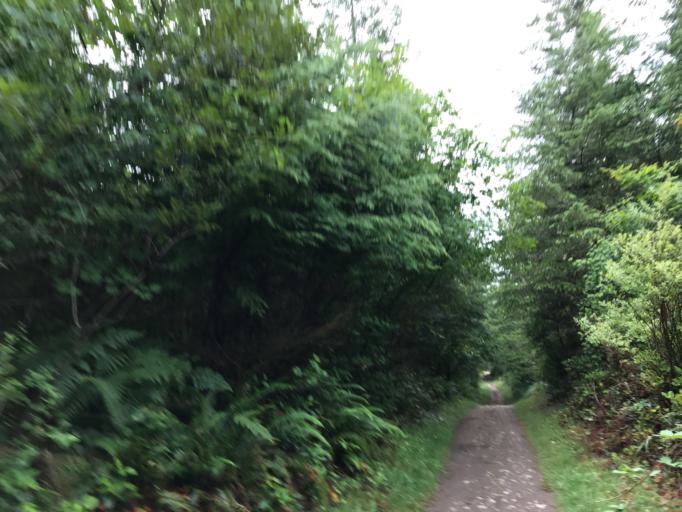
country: US
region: Washington
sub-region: King County
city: Ravensdale
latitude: 47.3391
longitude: -122.0069
